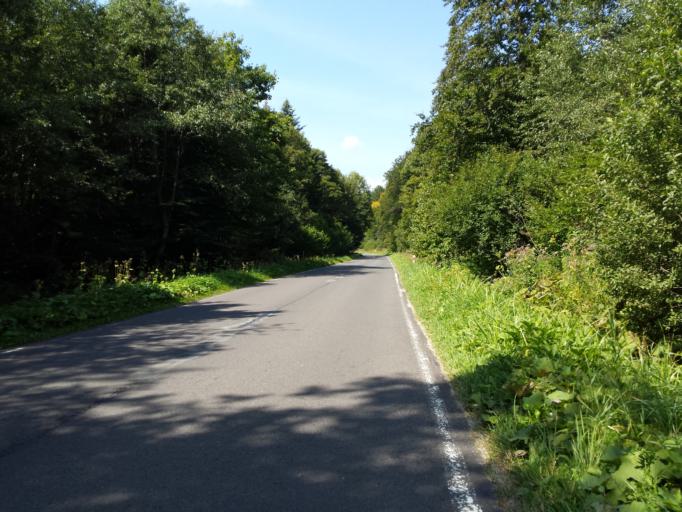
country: PL
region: Subcarpathian Voivodeship
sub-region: Powiat bieszczadzki
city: Lutowiska
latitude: 49.1116
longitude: 22.6197
